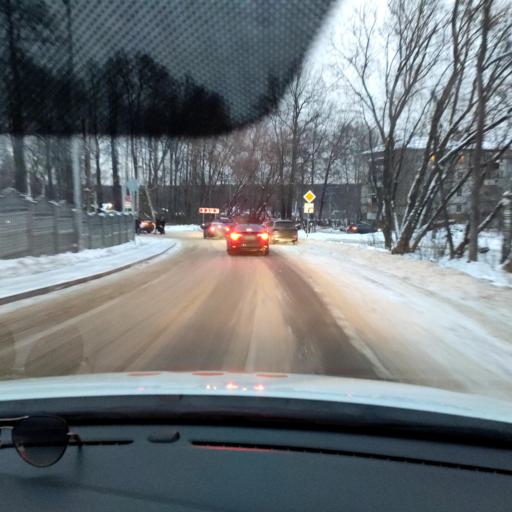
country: RU
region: Tatarstan
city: Vysokaya Gora
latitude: 55.9281
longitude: 49.2011
